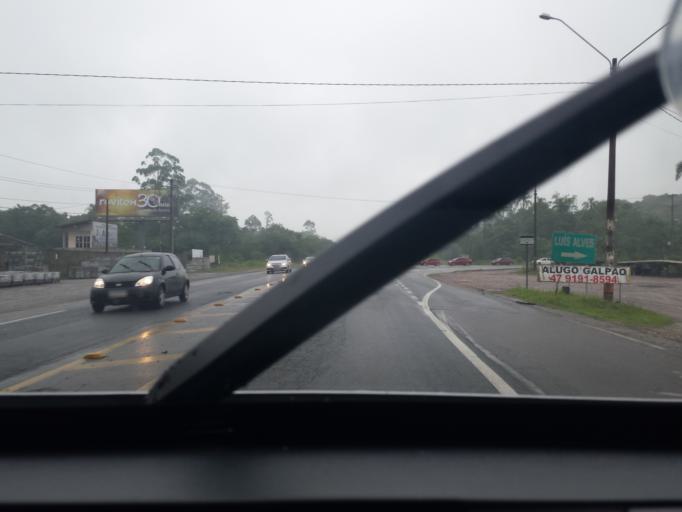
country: BR
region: Santa Catarina
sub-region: Navegantes
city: Navegantes
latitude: -26.8335
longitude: -48.7353
